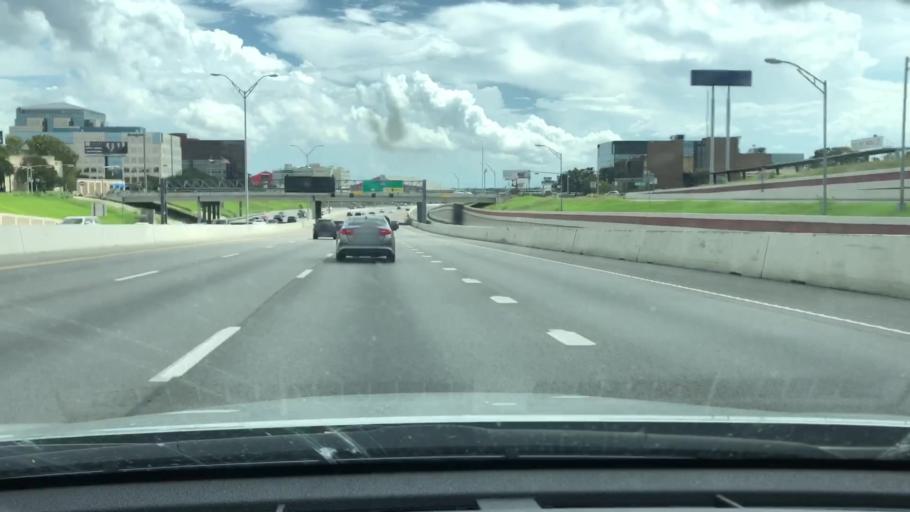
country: US
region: Texas
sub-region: Bexar County
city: Castle Hills
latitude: 29.5344
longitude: -98.4894
